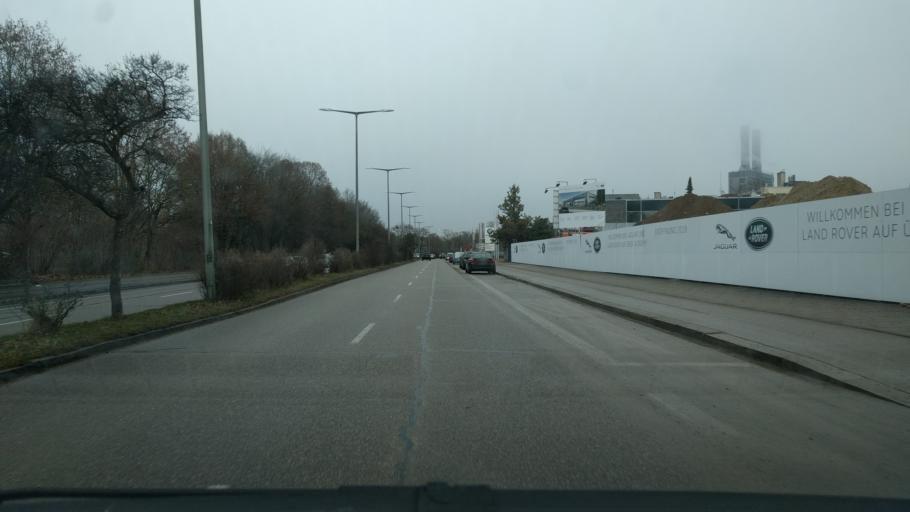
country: DE
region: Bavaria
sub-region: Upper Bavaria
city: Pullach im Isartal
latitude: 48.0906
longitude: 11.5030
